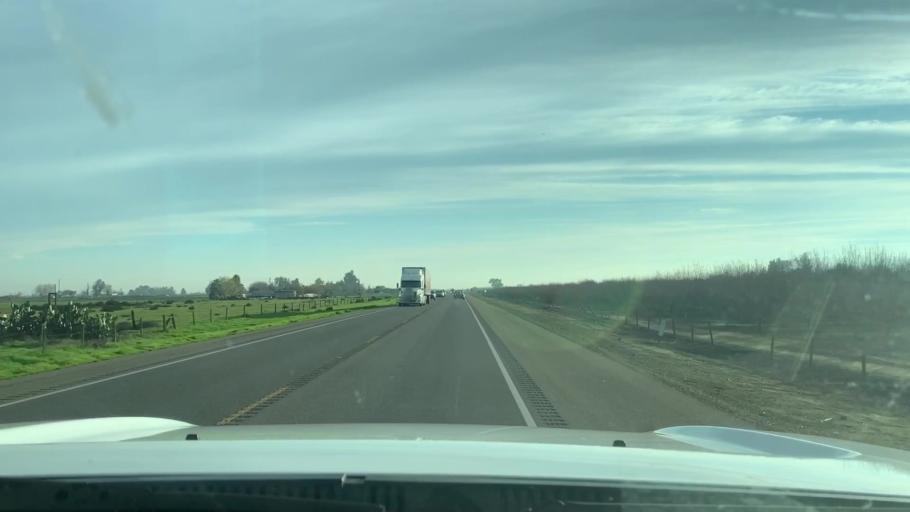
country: US
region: California
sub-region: Fresno County
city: Riverdale
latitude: 36.4205
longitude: -119.8034
